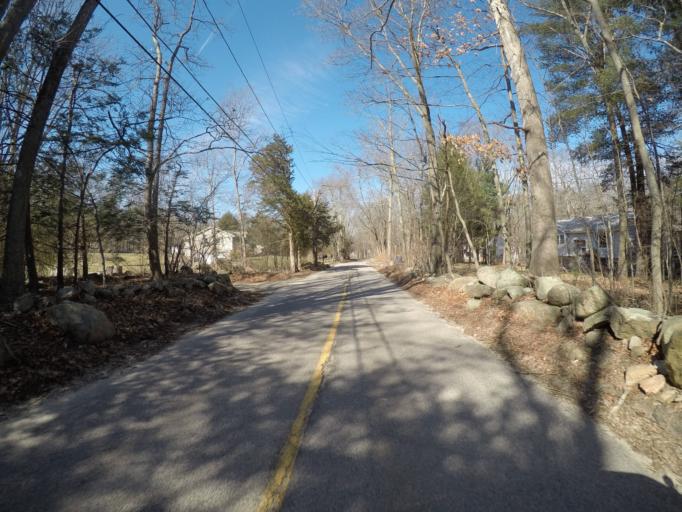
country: US
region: Massachusetts
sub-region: Norfolk County
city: Sharon
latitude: 42.0920
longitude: -71.1554
